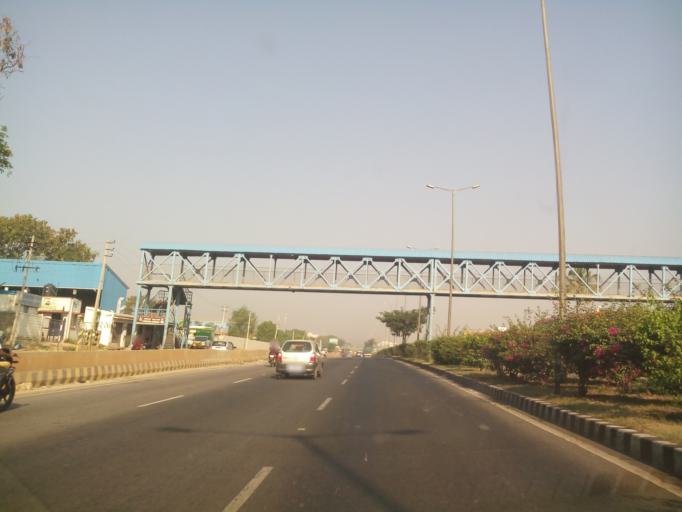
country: IN
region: Karnataka
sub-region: Bangalore Rural
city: Nelamangala
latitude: 13.0852
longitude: 77.4125
